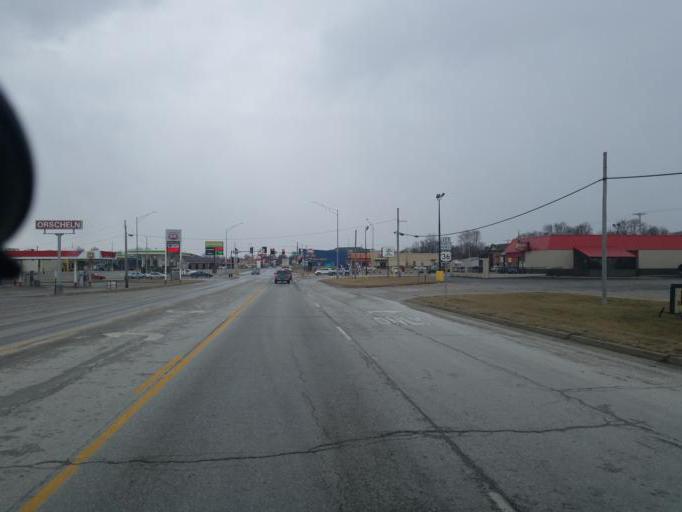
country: US
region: Missouri
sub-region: Macon County
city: Macon
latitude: 39.7532
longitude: -92.4679
